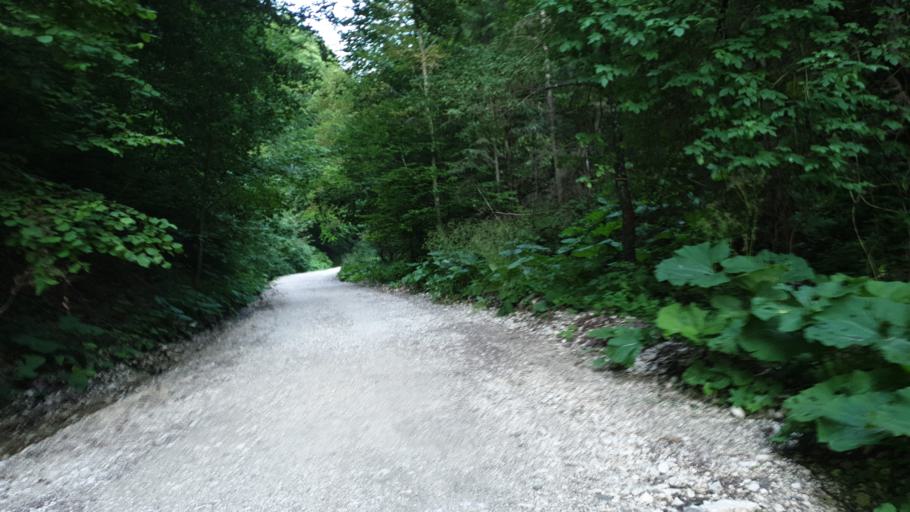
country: RO
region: Brasov
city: Brasov
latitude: 45.6118
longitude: 25.5656
